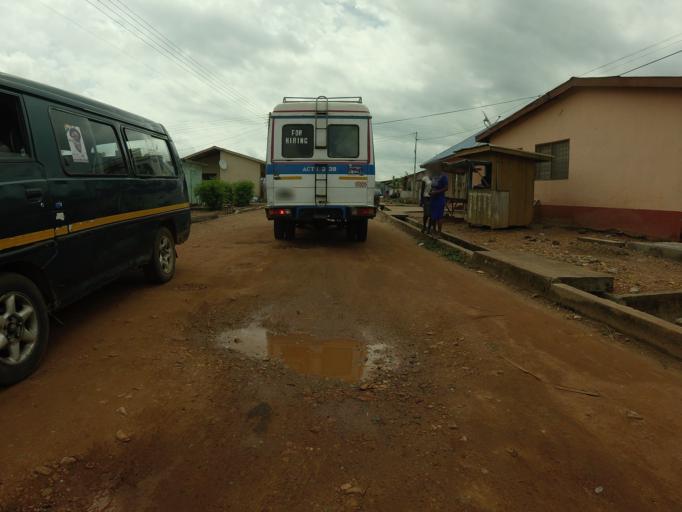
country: GH
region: Volta
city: Ho
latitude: 6.6019
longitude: 0.4693
